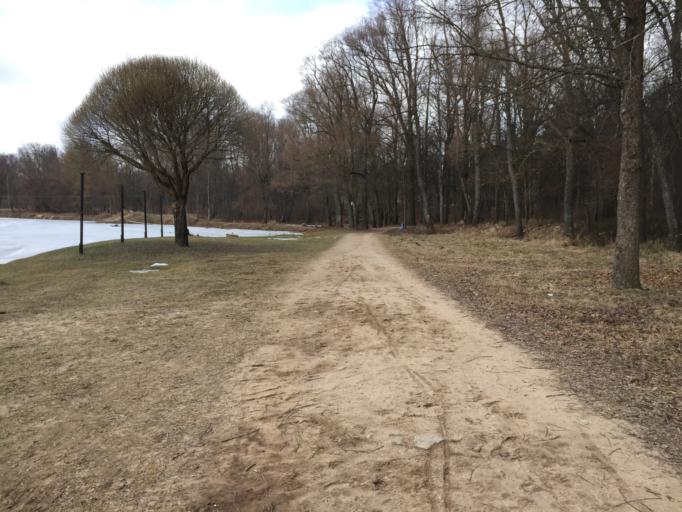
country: LV
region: Valmieras Rajons
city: Valmiera
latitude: 57.5366
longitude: 25.4350
